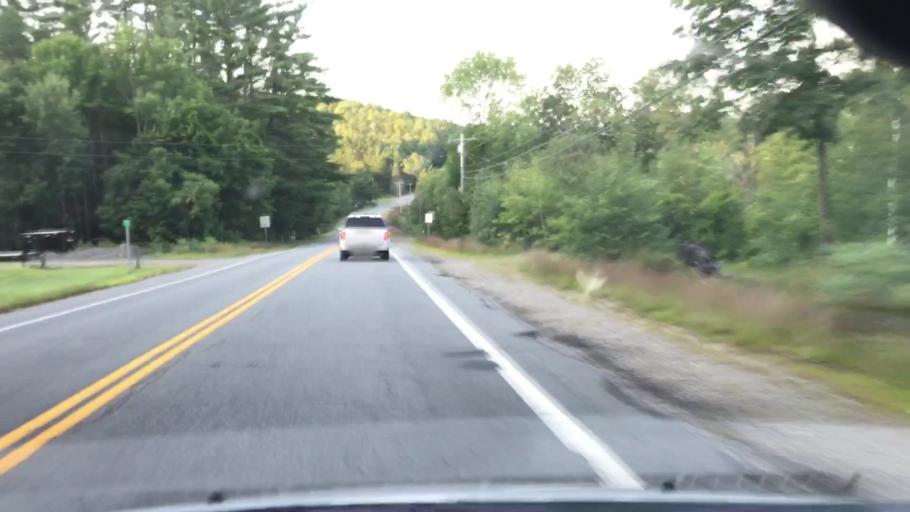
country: US
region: New Hampshire
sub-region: Grafton County
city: Rumney
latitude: 43.8778
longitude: -71.9115
